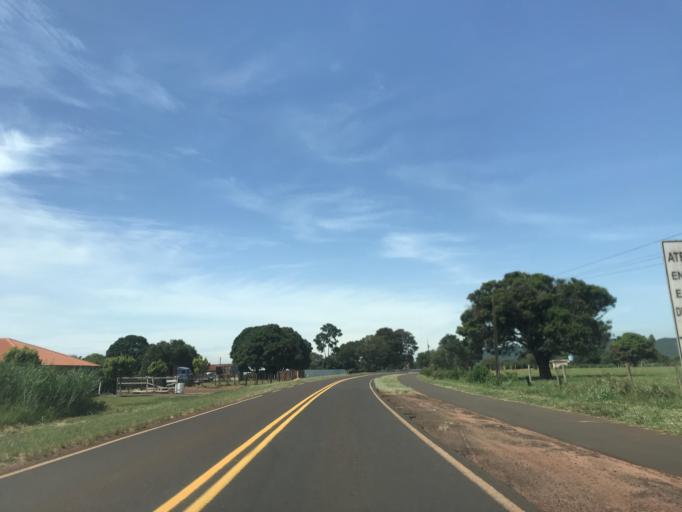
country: BR
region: Parana
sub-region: Terra Rica
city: Terra Rica
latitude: -22.7498
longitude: -52.6252
